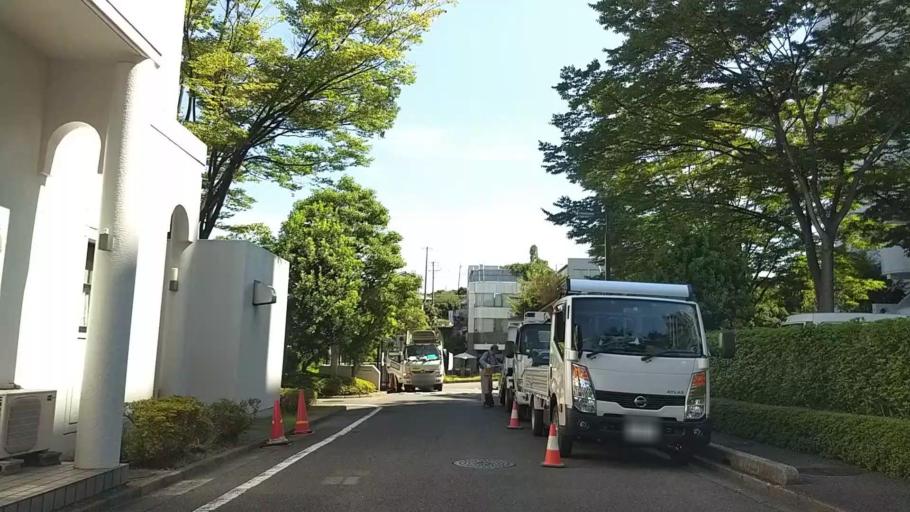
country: JP
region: Tokyo
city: Chofugaoka
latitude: 35.5660
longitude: 139.5678
